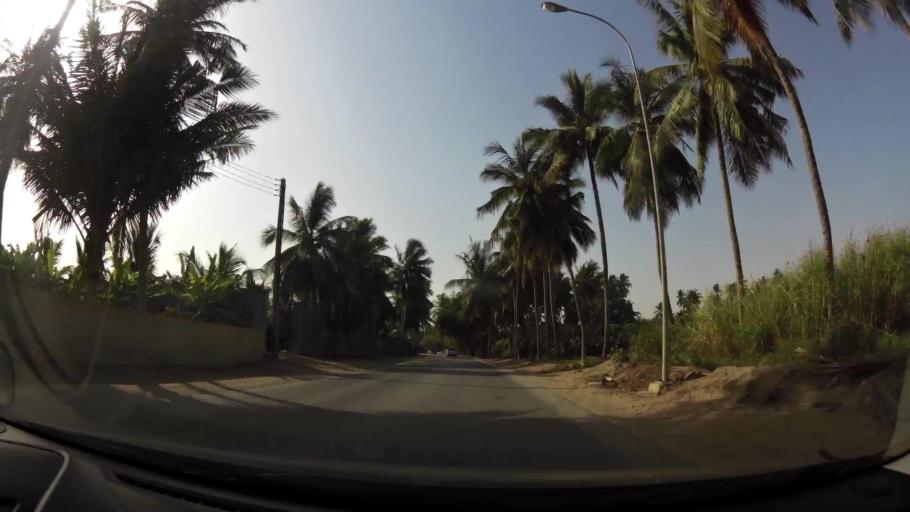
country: OM
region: Zufar
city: Salalah
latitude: 17.0045
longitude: 54.0988
